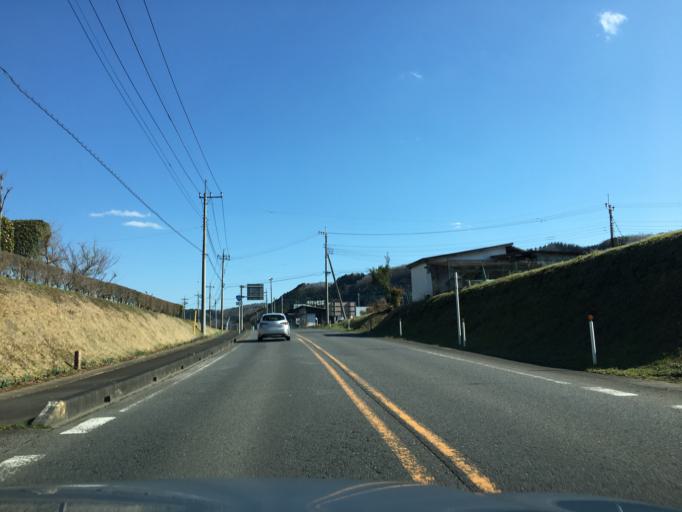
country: JP
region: Tochigi
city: Motegi
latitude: 36.5640
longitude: 140.2469
